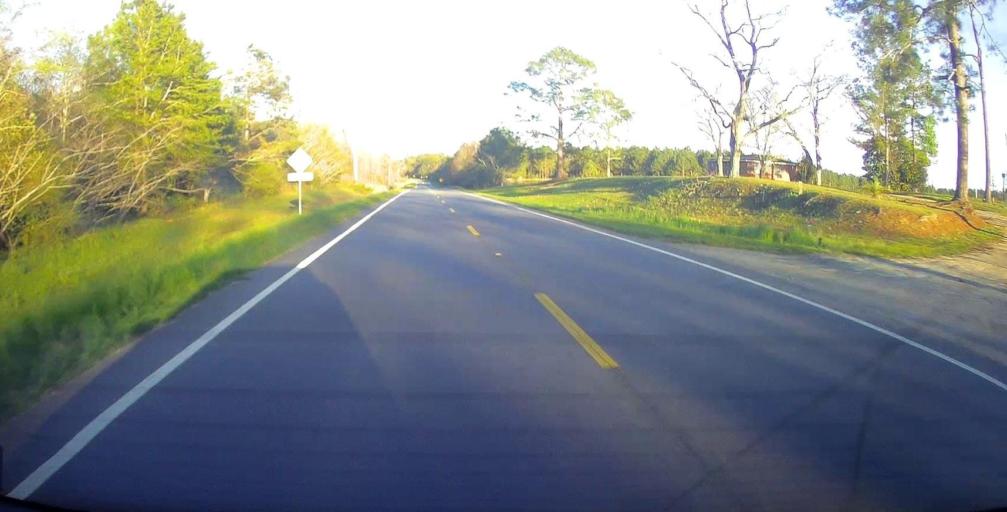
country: US
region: Georgia
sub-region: Wilcox County
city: Rochelle
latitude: 31.9453
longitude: -83.5219
